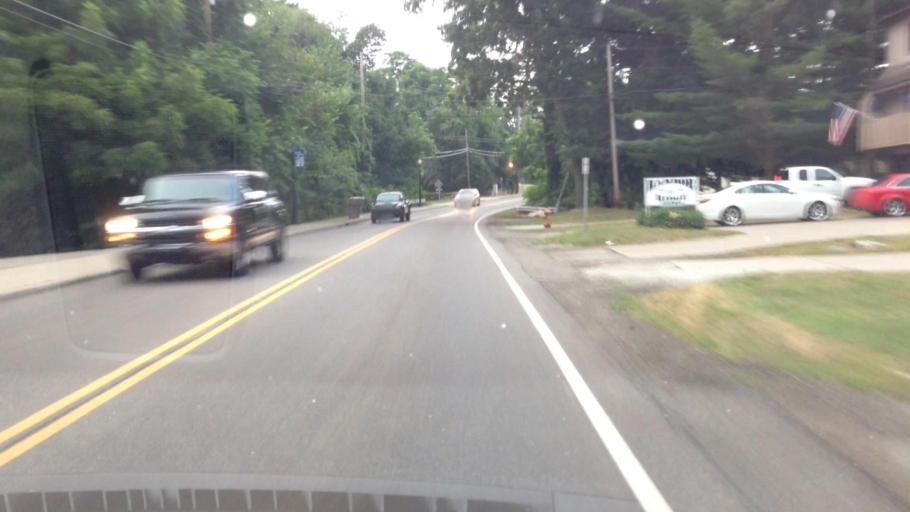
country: US
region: Ohio
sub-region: Summit County
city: Portage Lakes
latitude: 40.9991
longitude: -81.5397
